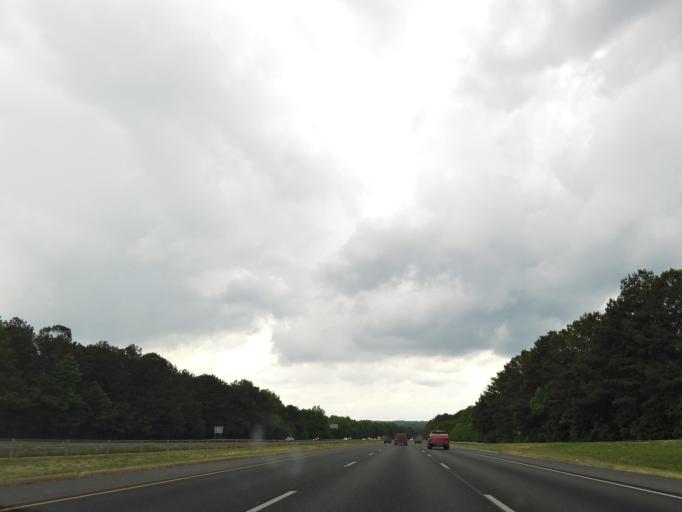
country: US
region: Georgia
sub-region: Carroll County
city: Villa Rica
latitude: 33.7194
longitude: -84.8351
